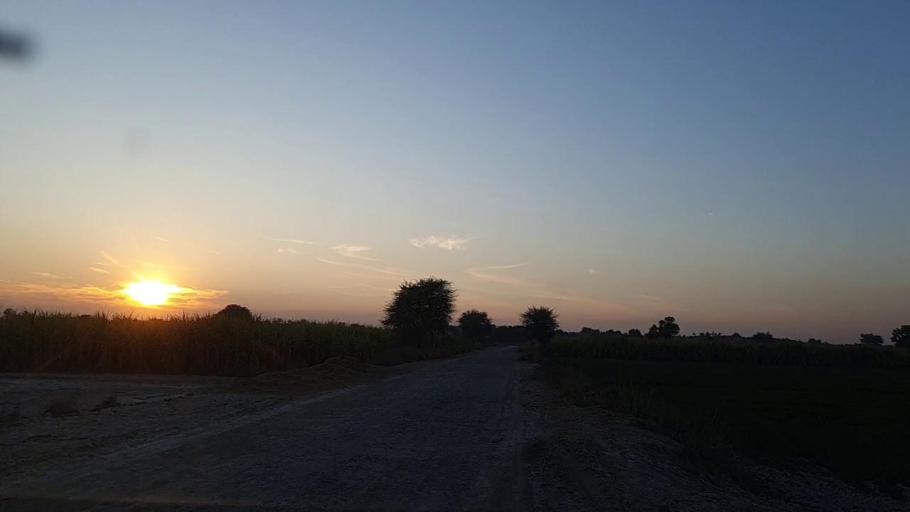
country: PK
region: Sindh
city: Bandhi
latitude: 26.6217
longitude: 68.3473
